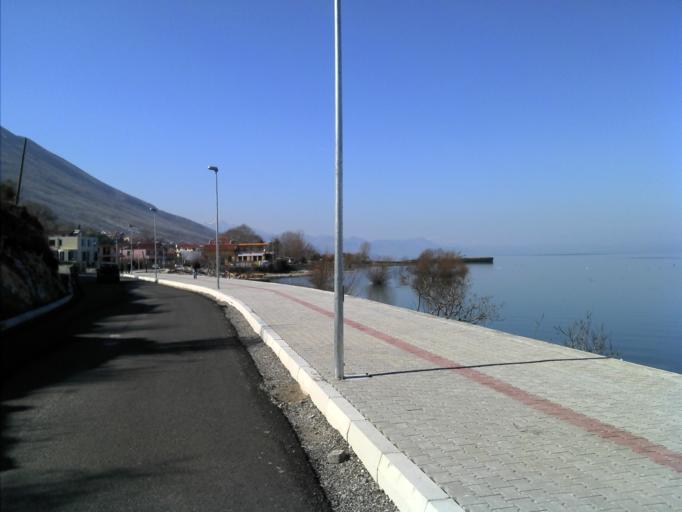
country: AL
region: Shkoder
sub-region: Rrethi i Shkodres
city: Berdica e Madhe
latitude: 42.0583
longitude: 19.4611
